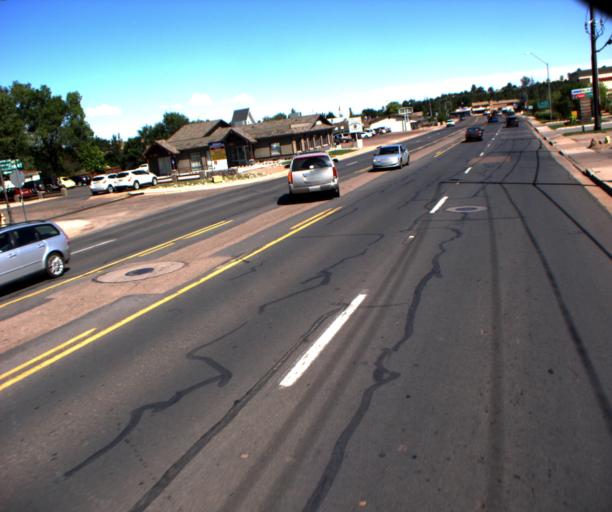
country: US
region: Arizona
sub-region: Navajo County
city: Show Low
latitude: 34.2514
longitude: -110.0285
